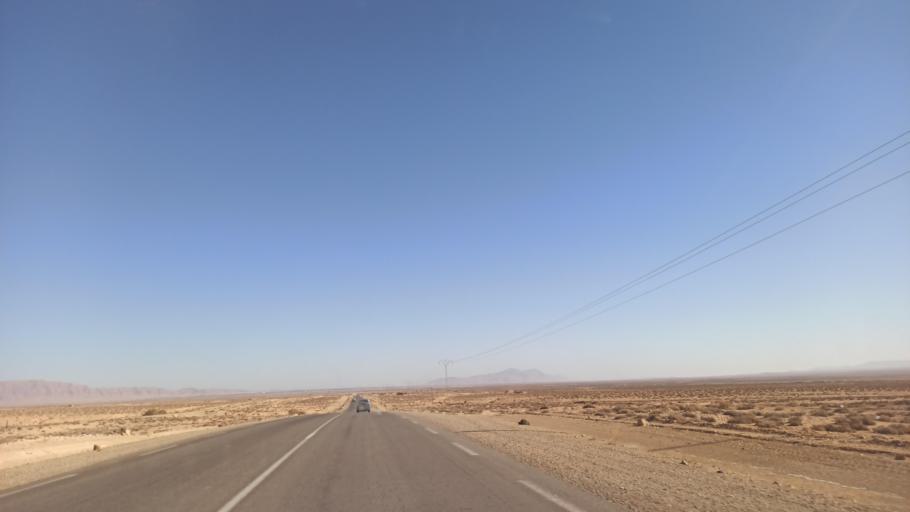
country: TN
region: Gafsa
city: Al Metlaoui
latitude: 34.3271
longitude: 8.5422
